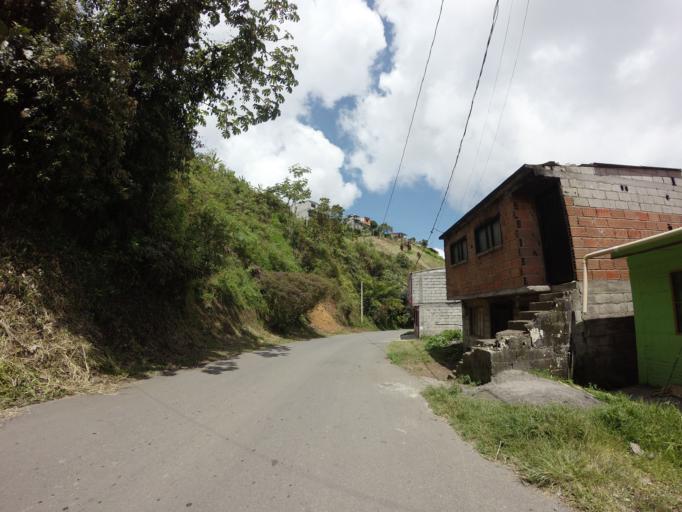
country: CO
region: Caldas
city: Marquetalia
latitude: 5.2960
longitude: -75.0475
